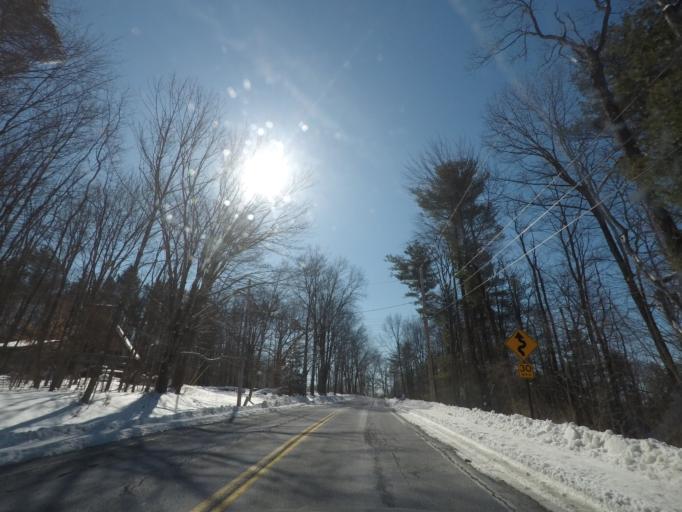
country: US
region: New York
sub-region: Saratoga County
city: Ballston Spa
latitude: 42.9955
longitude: -73.8266
